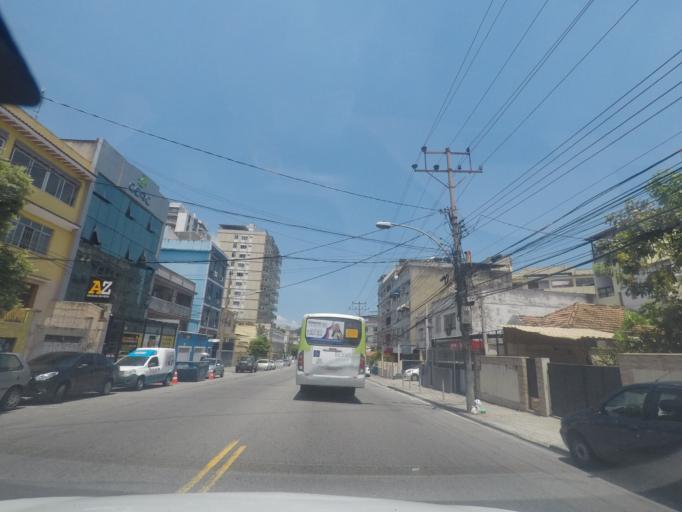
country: BR
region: Rio de Janeiro
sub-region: Duque De Caxias
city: Duque de Caxias
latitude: -22.8400
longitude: -43.3093
